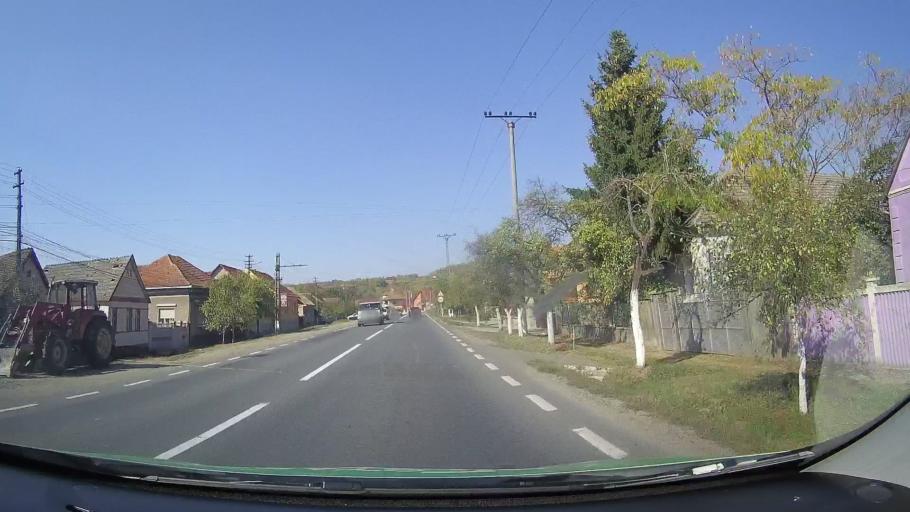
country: RO
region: Arad
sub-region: Oras Lipova
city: Radna
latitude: 46.0951
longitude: 21.6805
